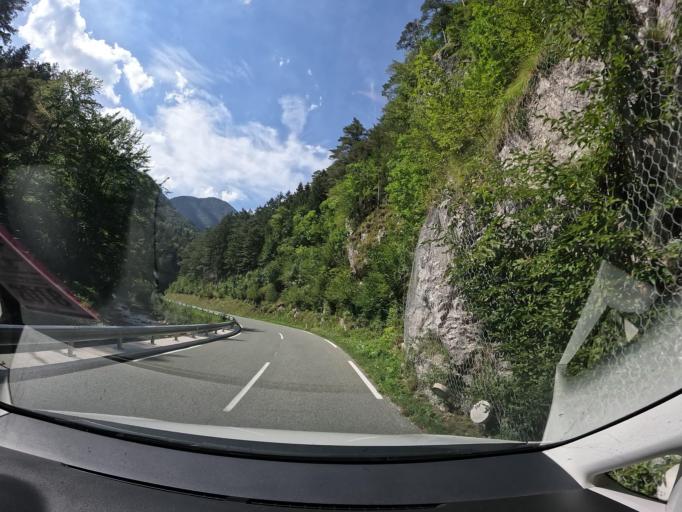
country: SI
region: Jezersko
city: Zgornje Jezersko
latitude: 46.3625
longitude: 14.4540
